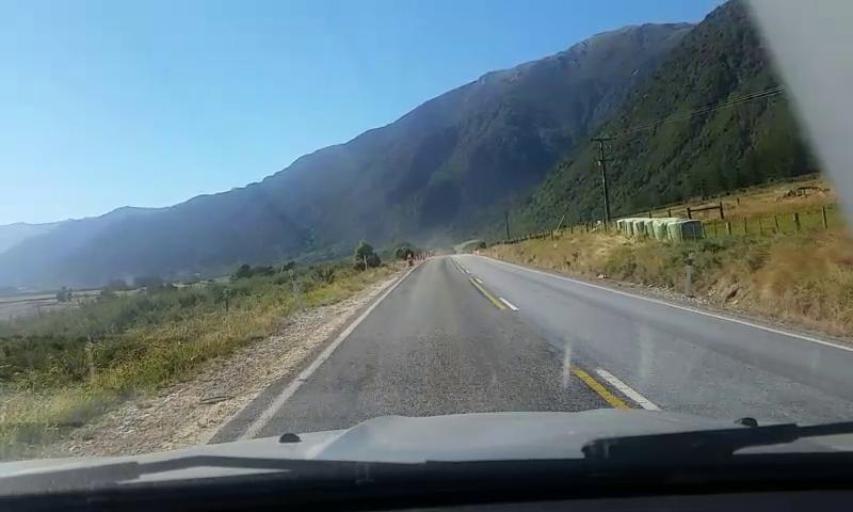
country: NZ
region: West Coast
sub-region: Grey District
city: Greymouth
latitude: -42.7482
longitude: 171.5394
